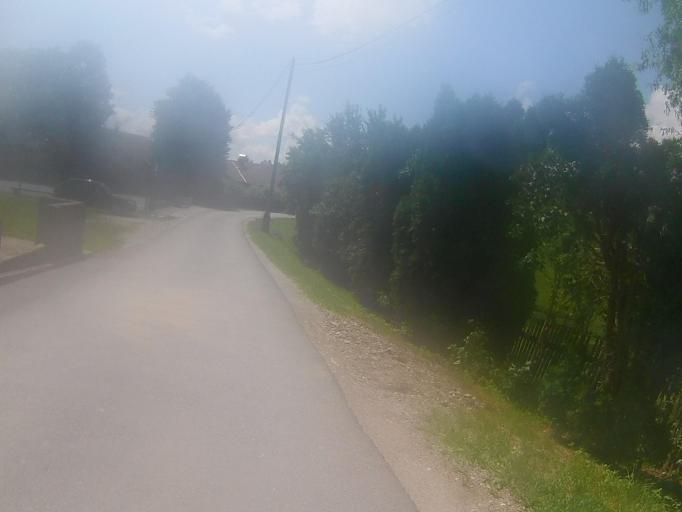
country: SI
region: Maribor
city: Bresternica
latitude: 46.6184
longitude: 15.5656
